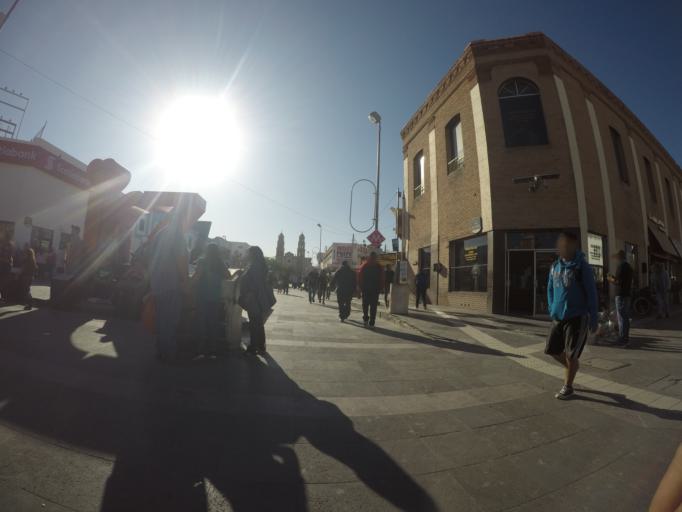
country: MX
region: Chihuahua
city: Ciudad Juarez
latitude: 31.7389
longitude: -106.4843
